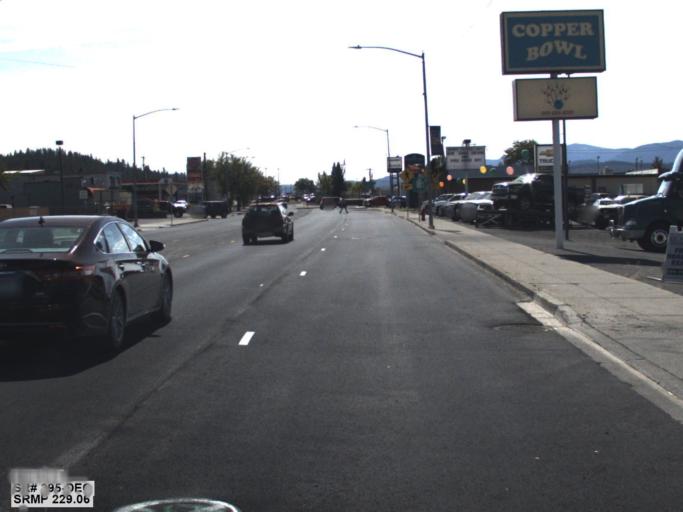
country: US
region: Washington
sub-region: Stevens County
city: Colville
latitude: 48.5382
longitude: -117.9057
